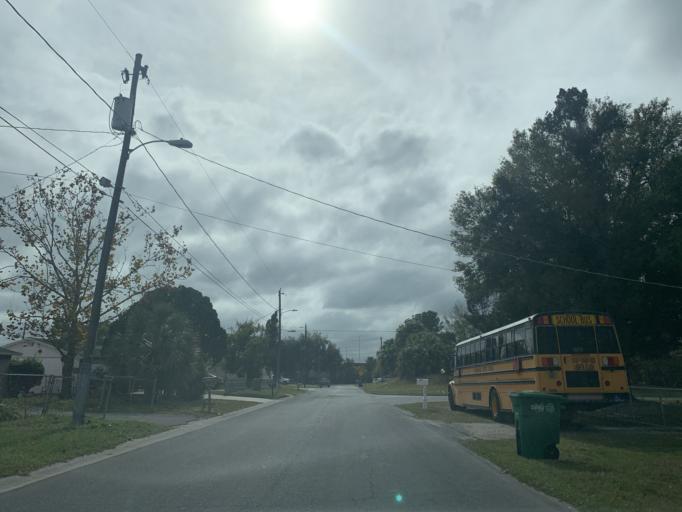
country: US
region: Florida
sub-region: Hillsborough County
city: East Lake-Orient Park
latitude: 27.9764
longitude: -82.3936
